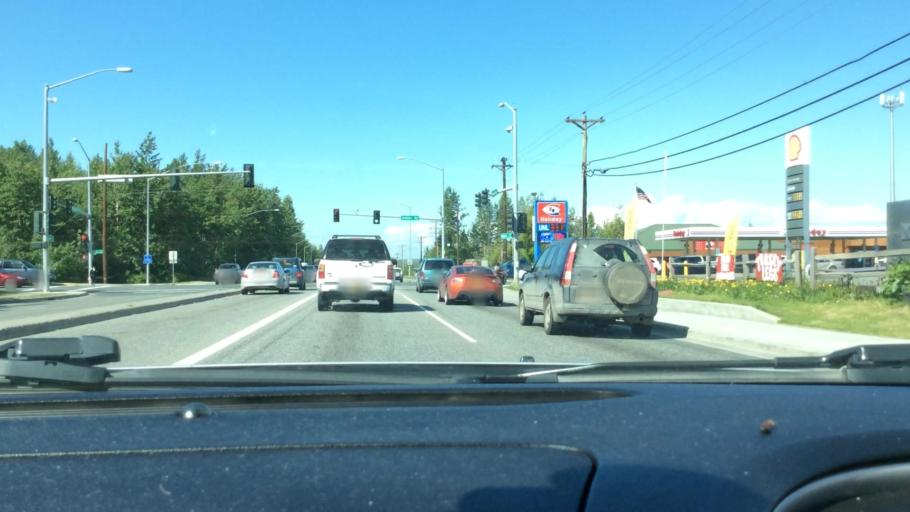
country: US
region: Alaska
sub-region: Anchorage Municipality
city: Anchorage
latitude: 61.2091
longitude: -149.7784
